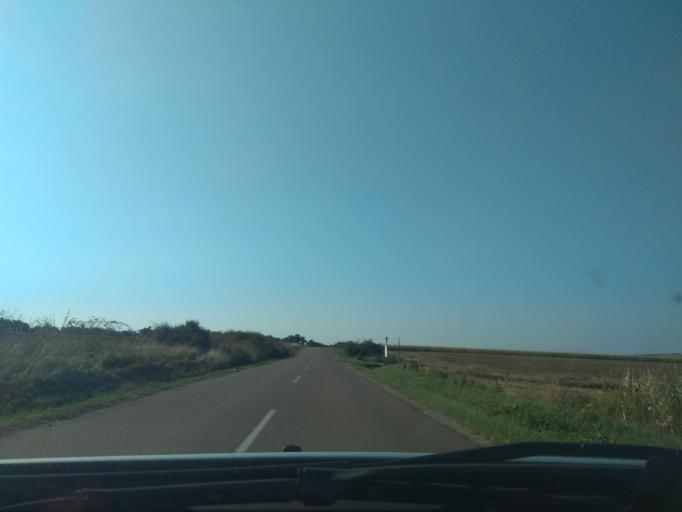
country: HU
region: Borsod-Abauj-Zemplen
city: Emod
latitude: 47.9648
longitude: 20.8013
